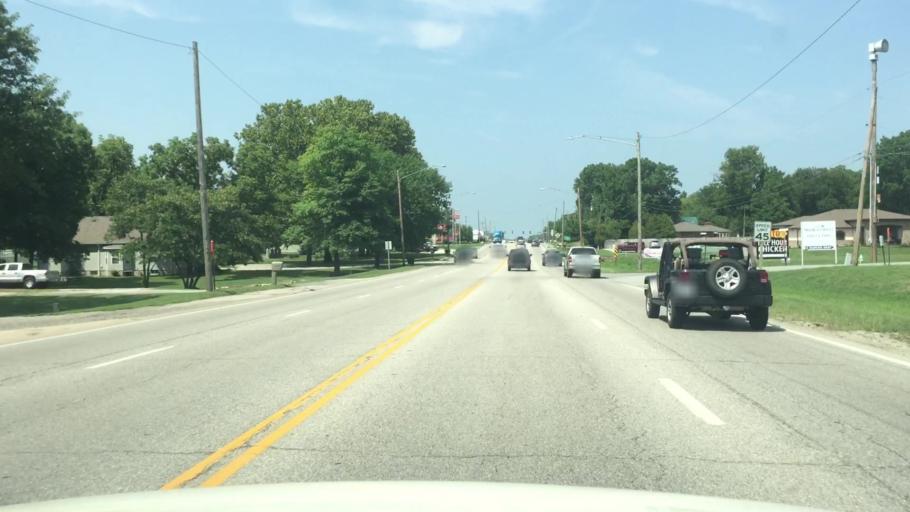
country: US
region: Kansas
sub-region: Crawford County
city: Frontenac
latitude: 37.4510
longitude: -94.7051
